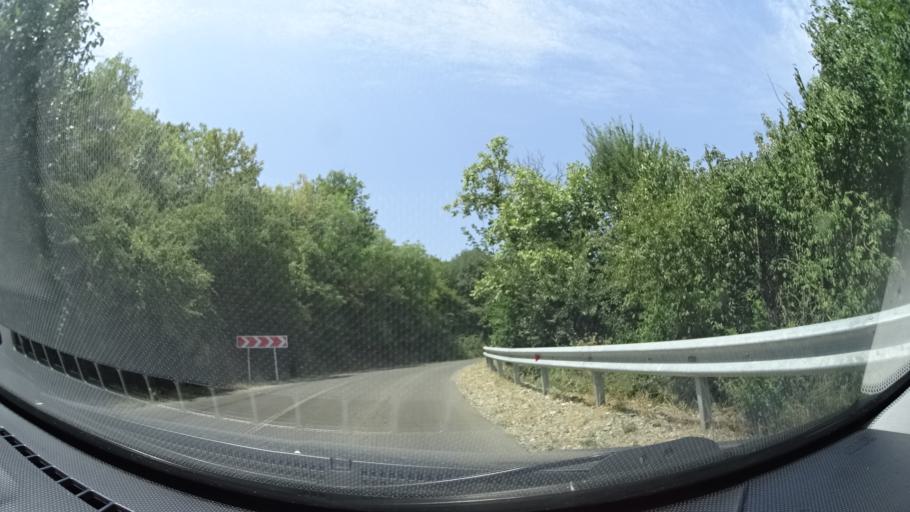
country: GE
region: Kakheti
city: Sighnaghi
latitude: 41.6244
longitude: 45.9338
